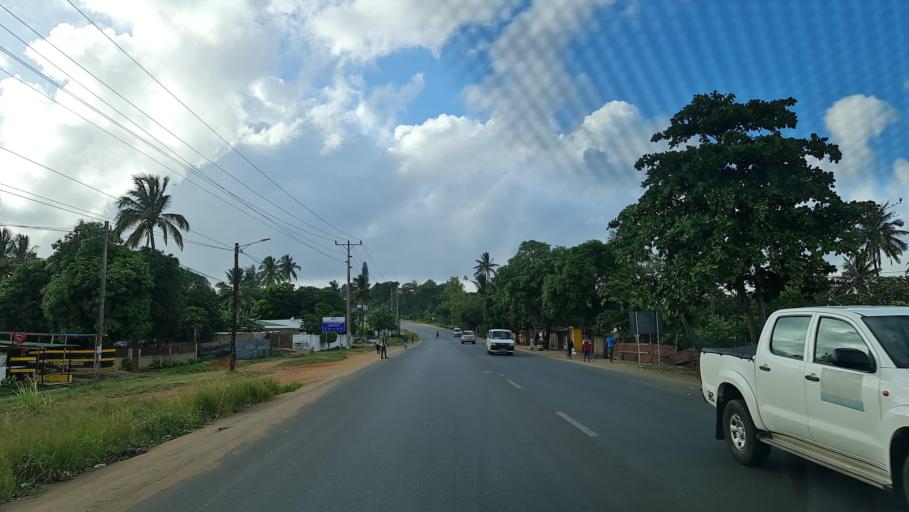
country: MZ
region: Gaza
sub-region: Xai-Xai District
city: Xai-Xai
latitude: -25.0536
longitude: 33.6493
